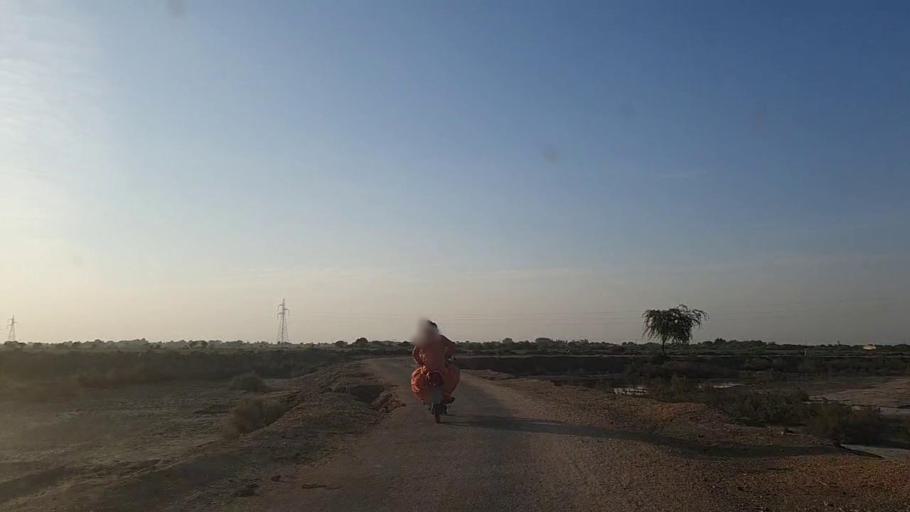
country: PK
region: Sindh
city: Mirpur Batoro
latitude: 24.6914
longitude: 68.2010
